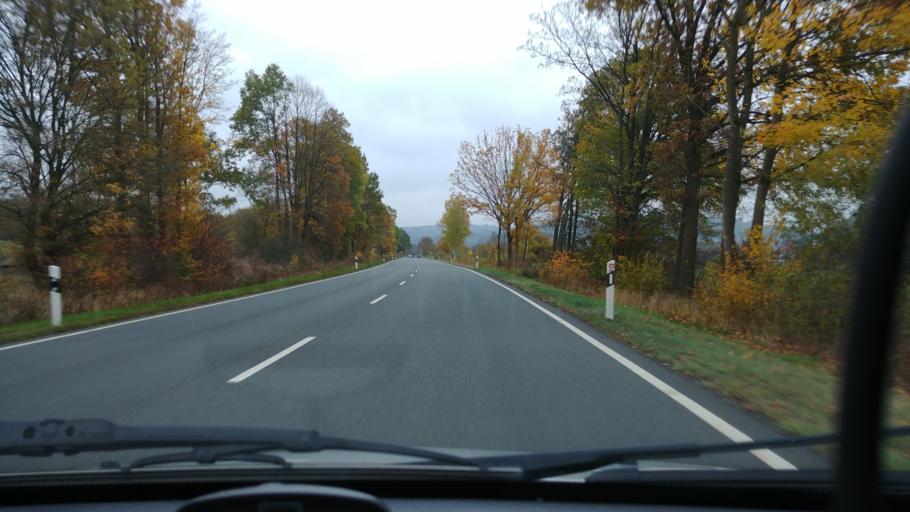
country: DE
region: Rheinland-Pfalz
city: Unnau
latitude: 50.6439
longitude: 7.8917
